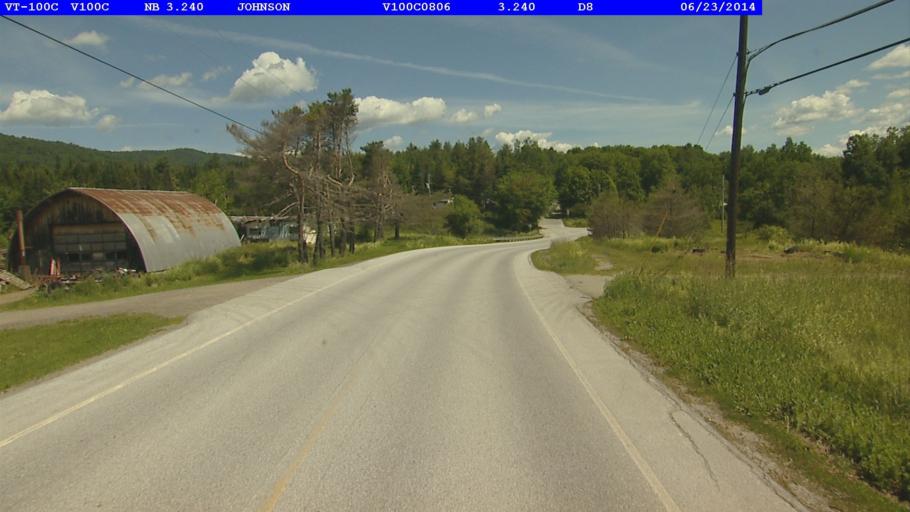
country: US
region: Vermont
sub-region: Lamoille County
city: Johnson
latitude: 44.6589
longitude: -72.6289
